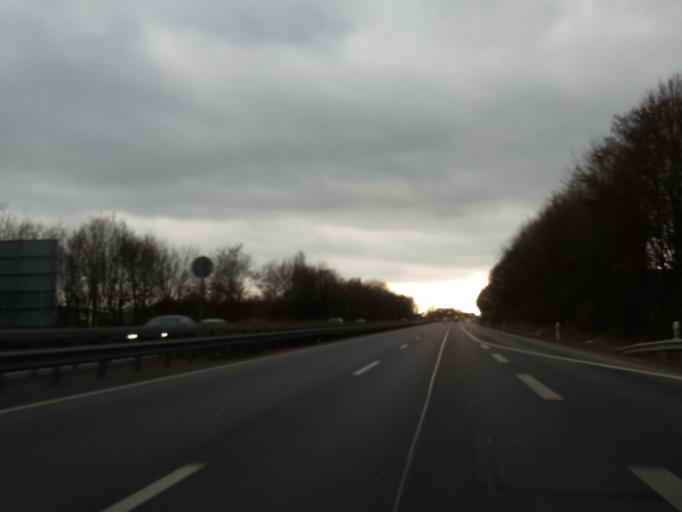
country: DE
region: Rheinland-Pfalz
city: Nieder-Olm
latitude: 49.9101
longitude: 8.1923
